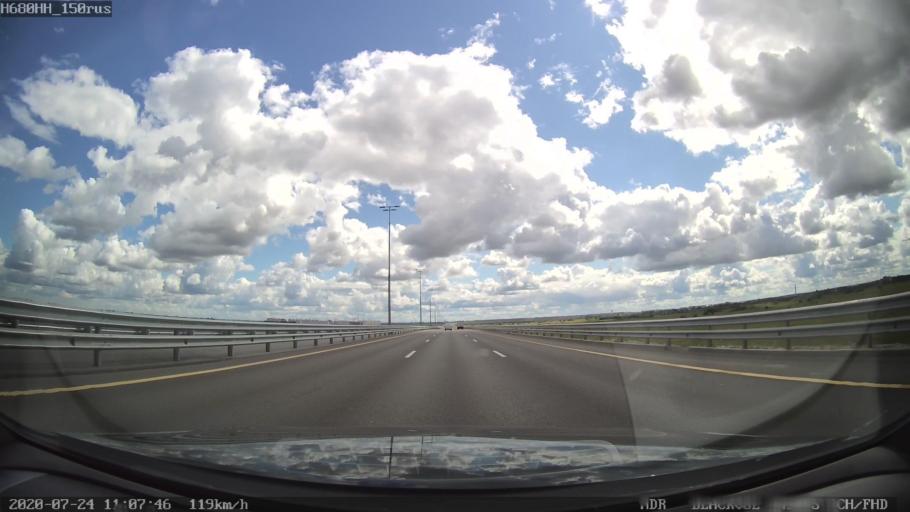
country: RU
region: St.-Petersburg
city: Pushkin
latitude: 59.7555
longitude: 30.4133
